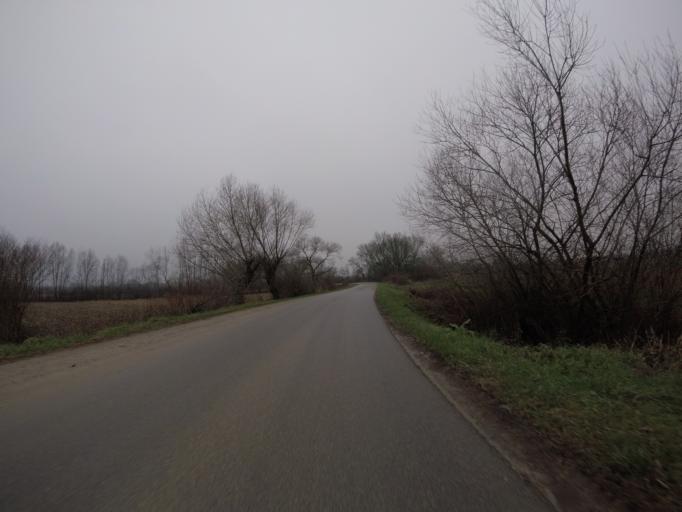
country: HR
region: Sisacko-Moslavacka
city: Lekenik
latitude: 45.6227
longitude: 16.3247
